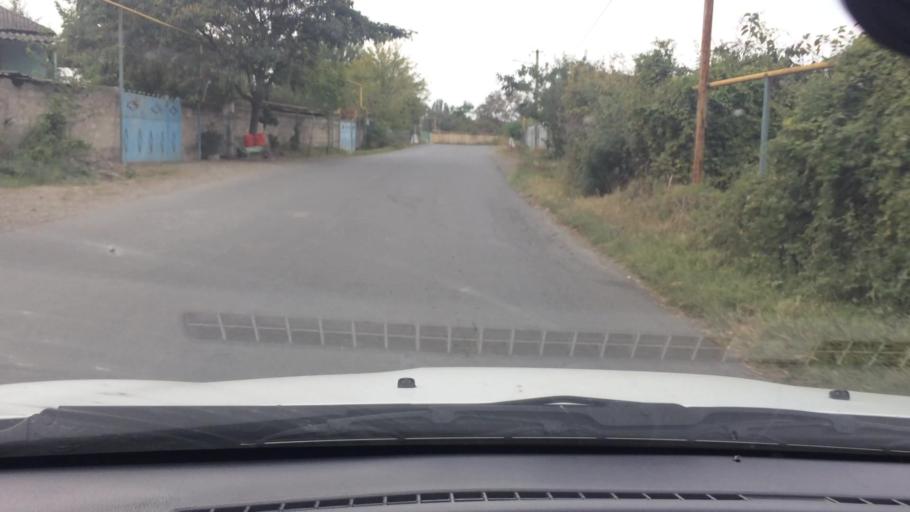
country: GE
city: Naghvarevi
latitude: 41.3515
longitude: 44.8639
